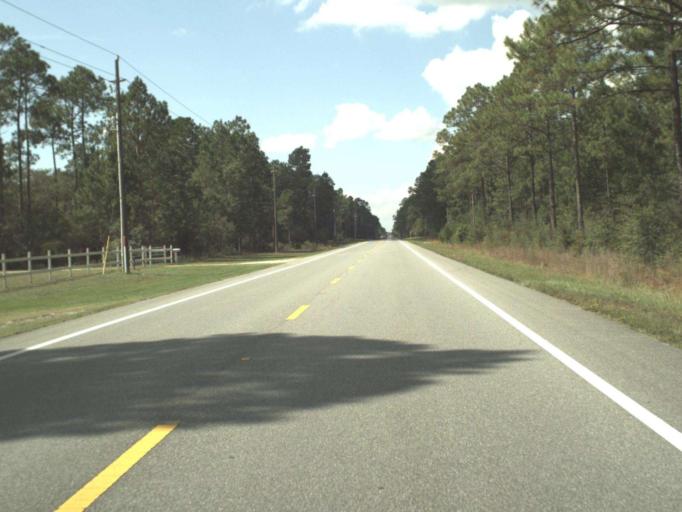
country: US
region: Florida
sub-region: Walton County
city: Freeport
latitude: 30.4763
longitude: -86.0278
